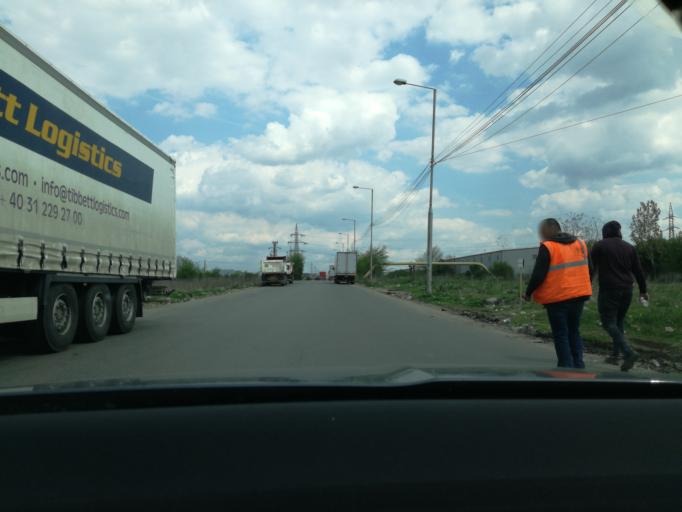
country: RO
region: Ilfov
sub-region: Comuna Chiajna
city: Chiajna
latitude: 44.4406
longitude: 25.9595
